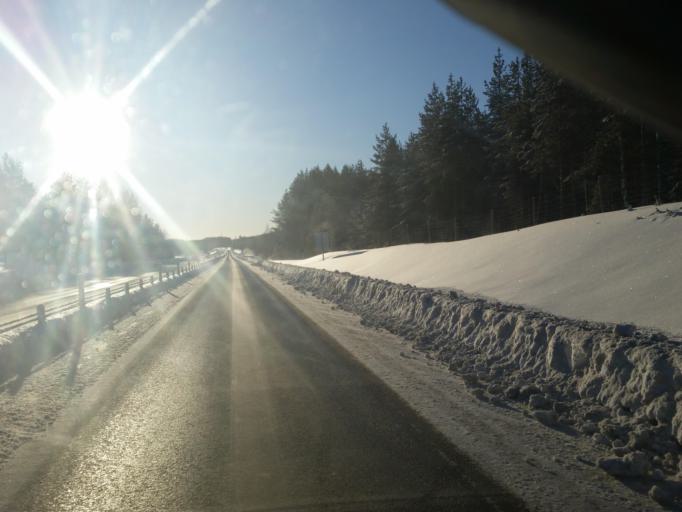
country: SE
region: Norrbotten
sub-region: Pitea Kommun
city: Pitea
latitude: 65.2667
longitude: 21.4598
